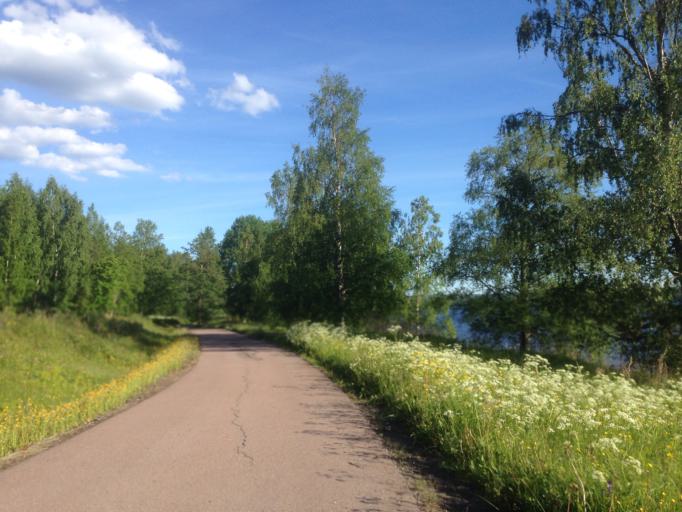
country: SE
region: Dalarna
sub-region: Ludvika Kommun
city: Ludvika
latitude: 60.1122
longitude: 15.2062
